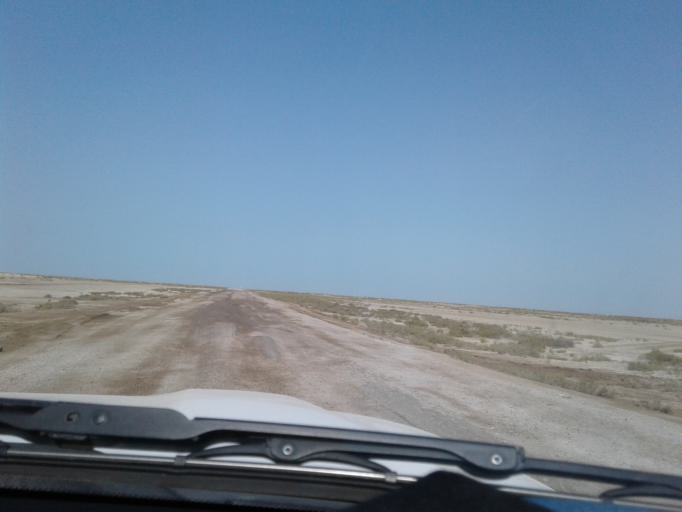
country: IR
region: Golestan
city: Gomishan
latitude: 37.8390
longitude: 53.8961
